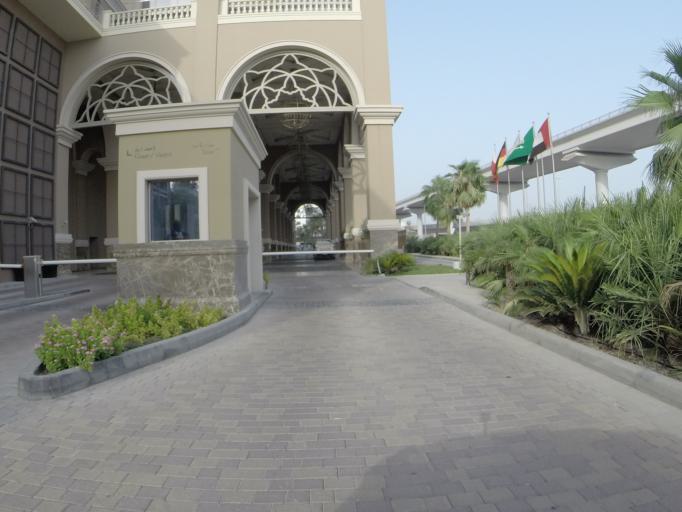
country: AE
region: Dubai
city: Dubai
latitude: 25.1192
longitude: 55.1981
